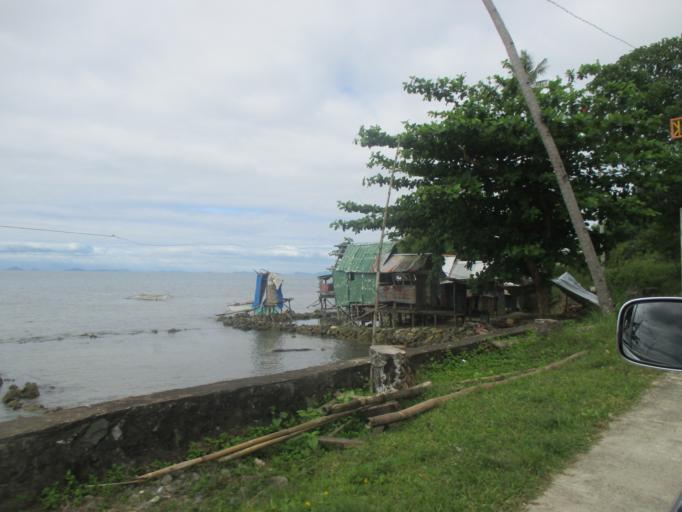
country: PH
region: Eastern Visayas
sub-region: Province of Eastern Samar
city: Lawa-an
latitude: 11.1114
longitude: 125.2112
